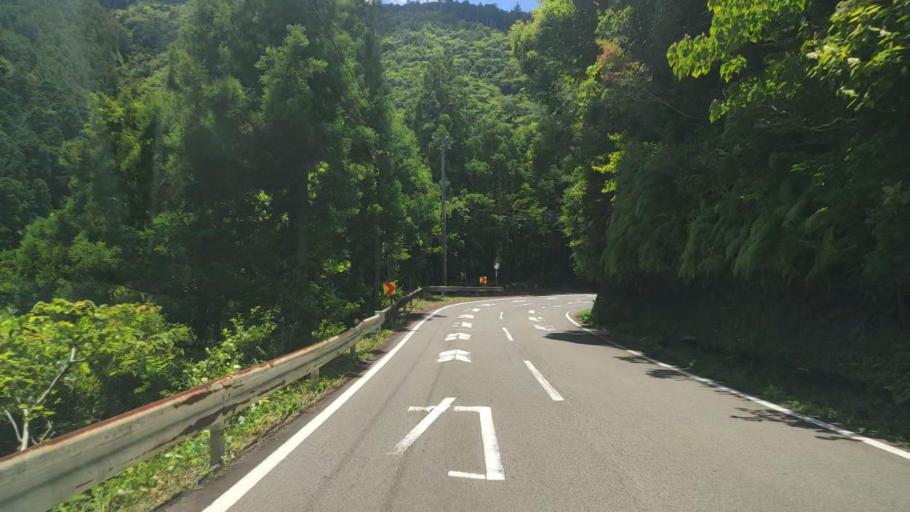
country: JP
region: Mie
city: Owase
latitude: 33.9957
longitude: 136.0137
